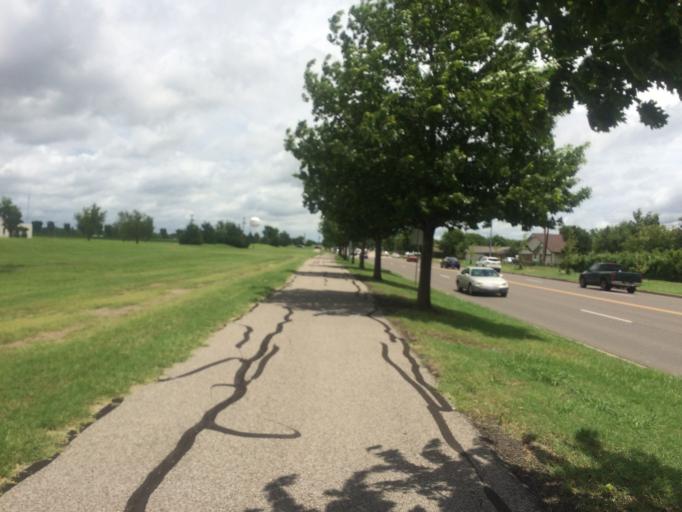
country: US
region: Oklahoma
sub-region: Cleveland County
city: Norman
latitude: 35.2331
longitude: -97.4626
